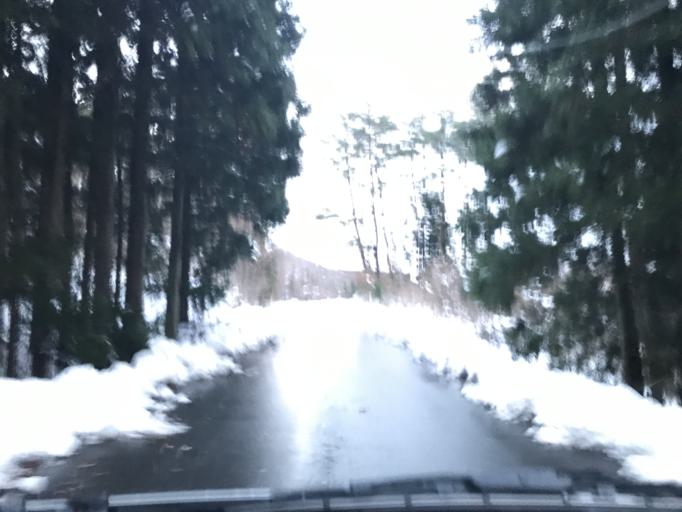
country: JP
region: Iwate
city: Mizusawa
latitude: 39.0491
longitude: 141.0211
